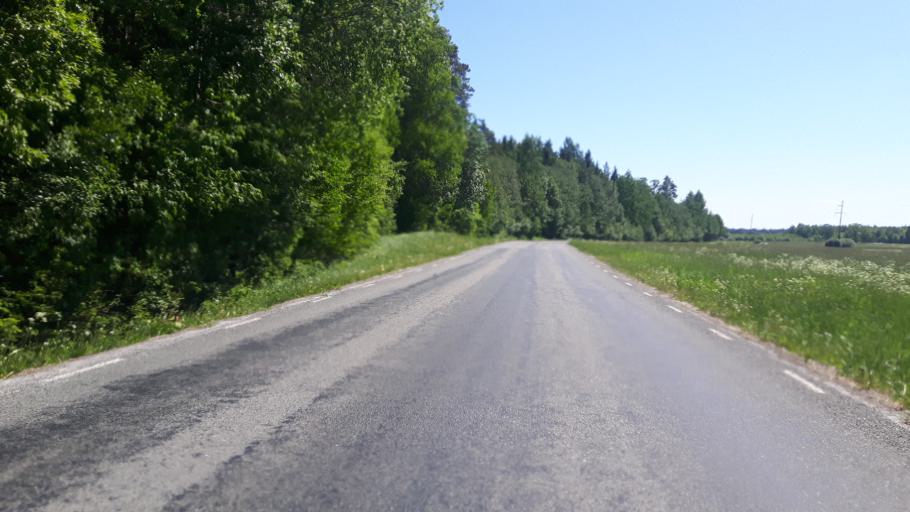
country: EE
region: Raplamaa
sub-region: Kohila vald
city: Kohila
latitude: 59.2072
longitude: 24.6868
